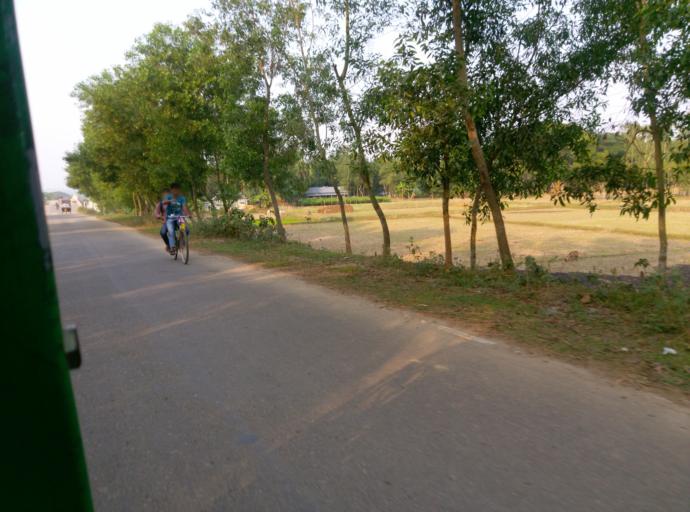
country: BD
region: Dhaka
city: Netrakona
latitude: 25.1483
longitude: 90.6593
